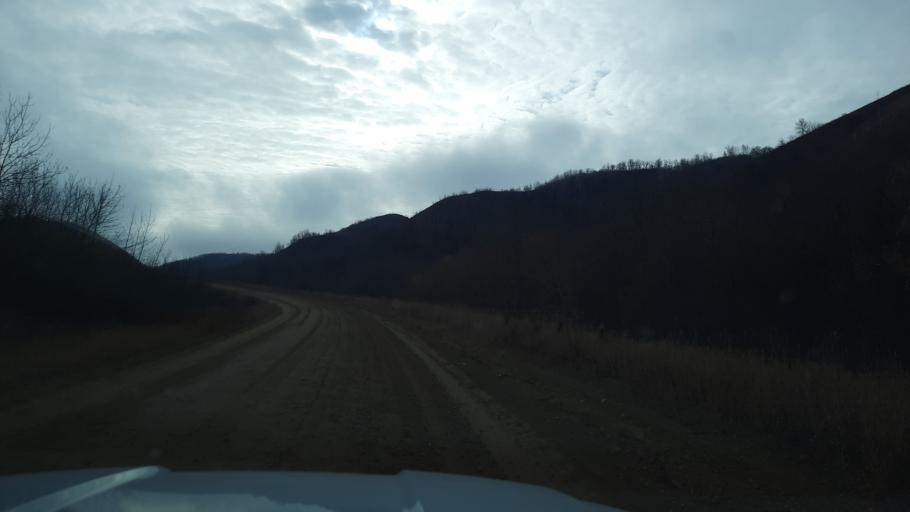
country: CA
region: Saskatchewan
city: White City
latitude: 50.7740
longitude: -104.1344
